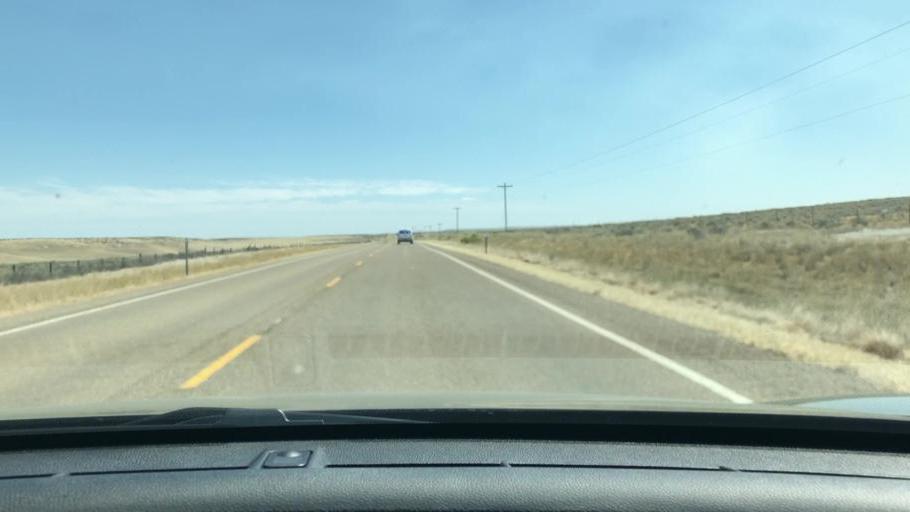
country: US
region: Idaho
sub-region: Owyhee County
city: Homedale
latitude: 42.8545
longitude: -117.5868
